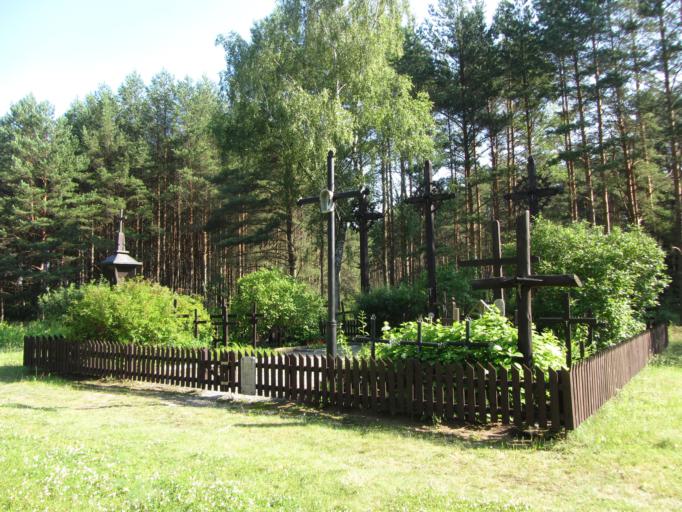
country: LT
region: Vilnius County
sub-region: Trakai
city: Rudiskes
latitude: 54.3993
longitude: 24.9585
